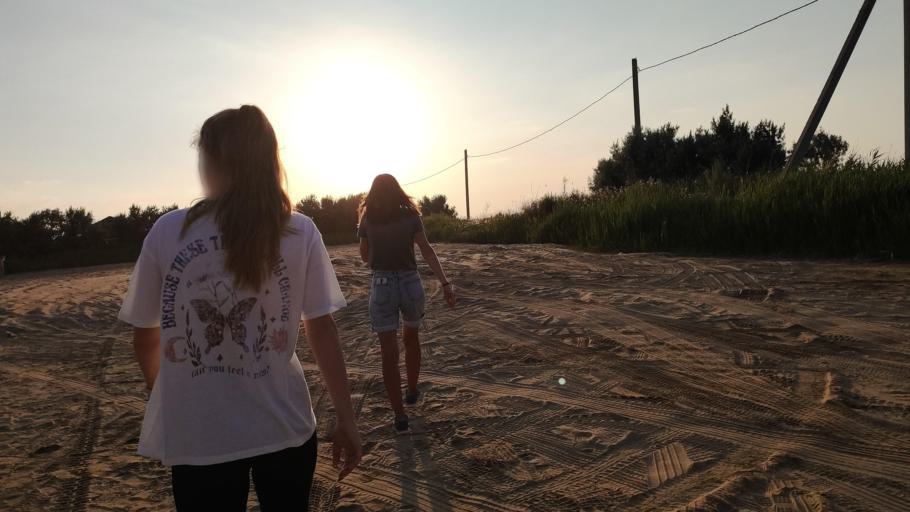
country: RU
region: Krasnodarskiy
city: Blagovetschenskaya
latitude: 45.0665
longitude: 37.0402
